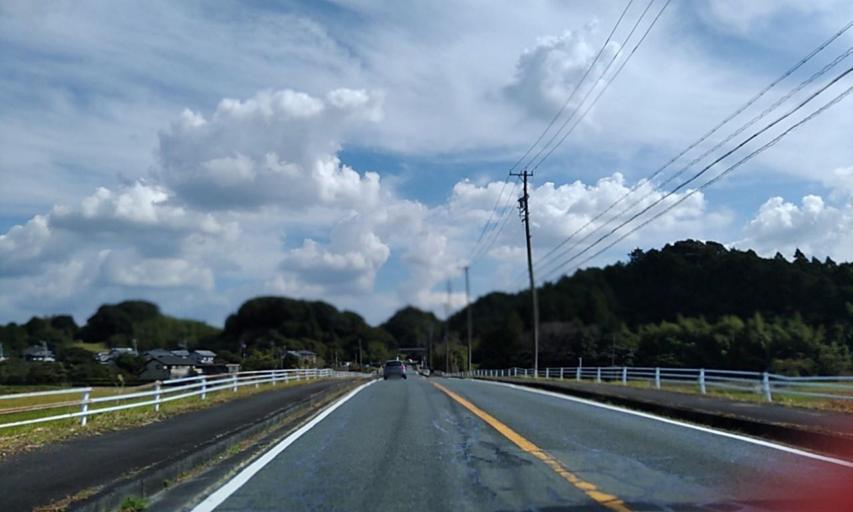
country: JP
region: Shizuoka
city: Mori
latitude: 34.8247
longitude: 137.8981
